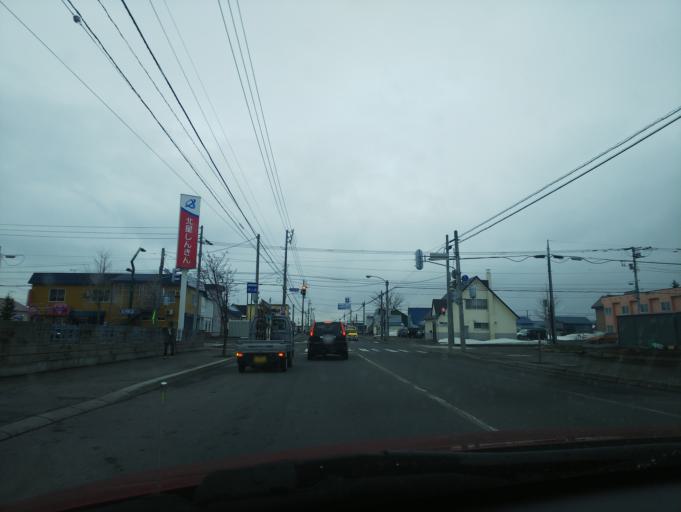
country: JP
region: Hokkaido
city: Nayoro
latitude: 44.3517
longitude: 142.4503
